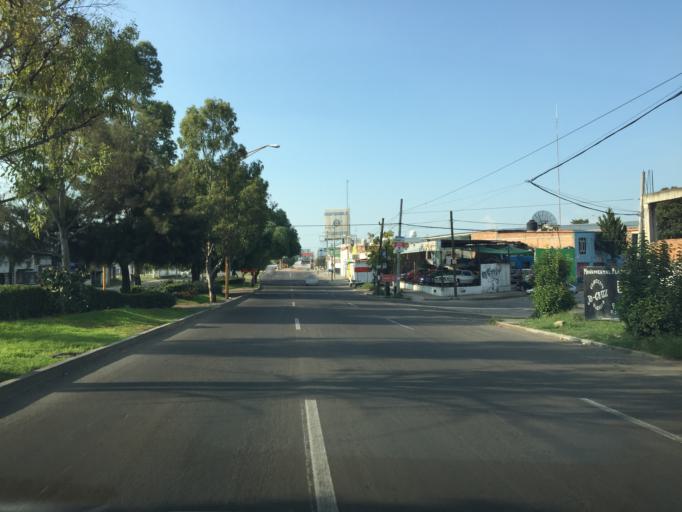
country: MX
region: Aguascalientes
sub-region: Aguascalientes
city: La Loma de los Negritos
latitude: 21.8659
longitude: -102.3177
